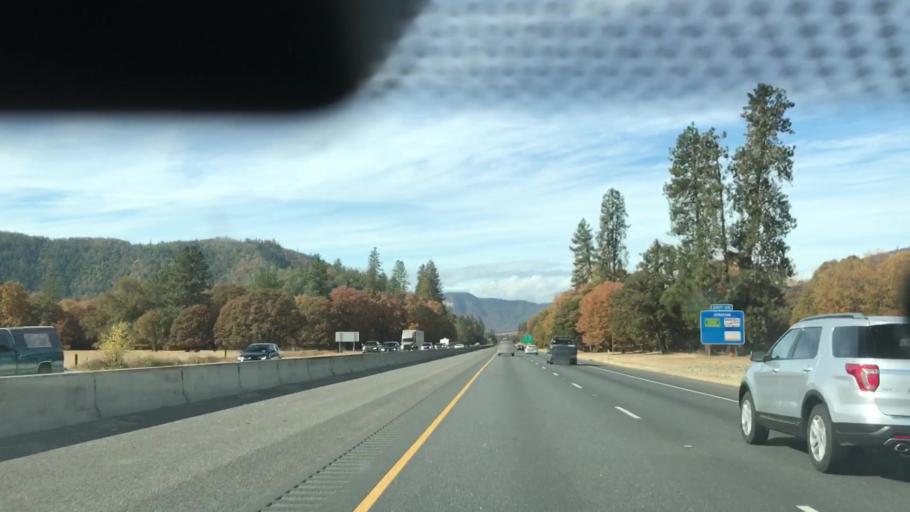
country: US
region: Oregon
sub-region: Jackson County
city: Gold Hill
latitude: 42.4216
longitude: -123.0252
